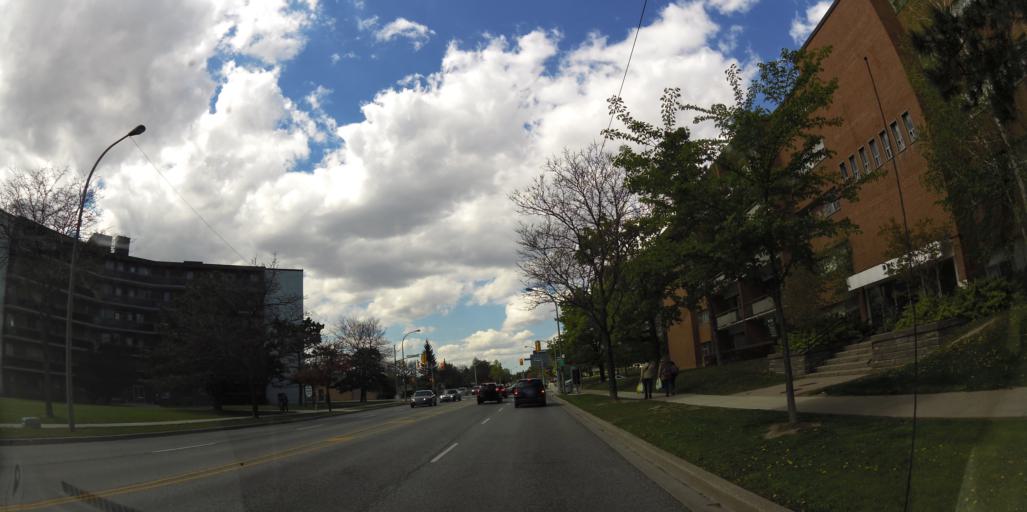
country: CA
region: Ontario
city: Etobicoke
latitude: 43.6388
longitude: -79.5645
